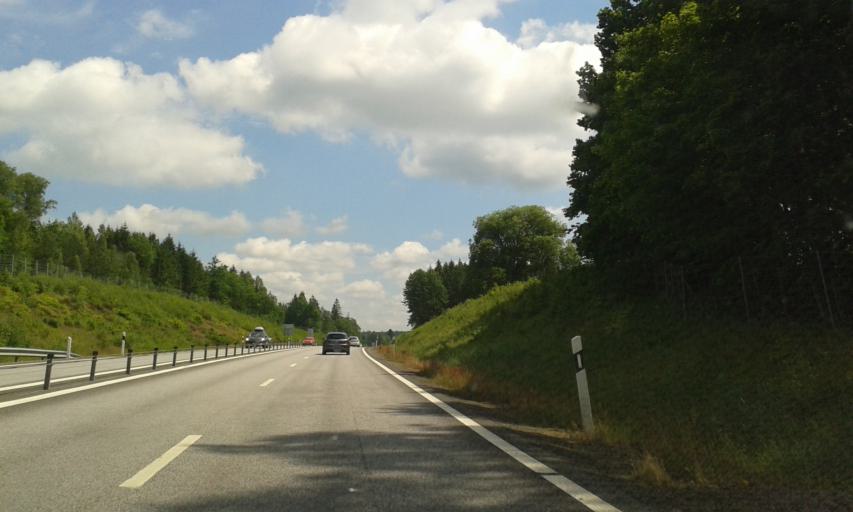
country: SE
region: Kronoberg
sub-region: Alvesta Kommun
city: Alvesta
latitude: 56.9207
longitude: 14.5982
